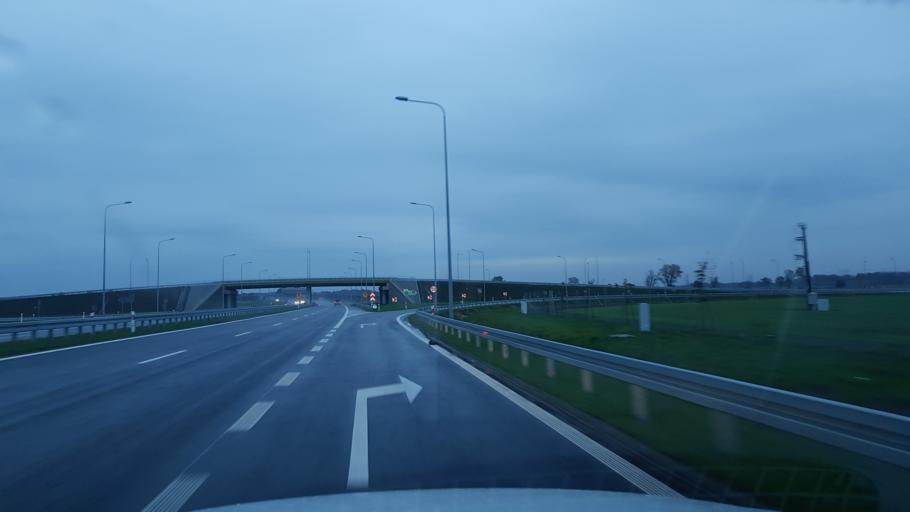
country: PL
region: West Pomeranian Voivodeship
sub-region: Powiat gryficki
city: Brojce
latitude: 53.8768
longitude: 15.3736
